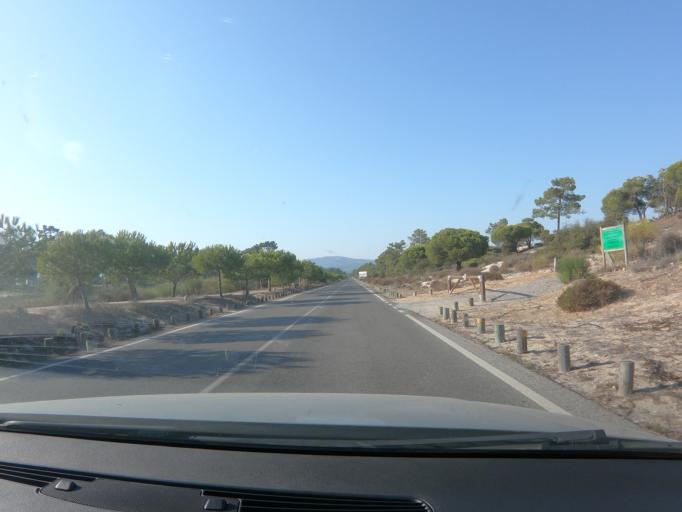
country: PT
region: Setubal
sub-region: Setubal
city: Setubal
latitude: 38.4769
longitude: -8.8875
